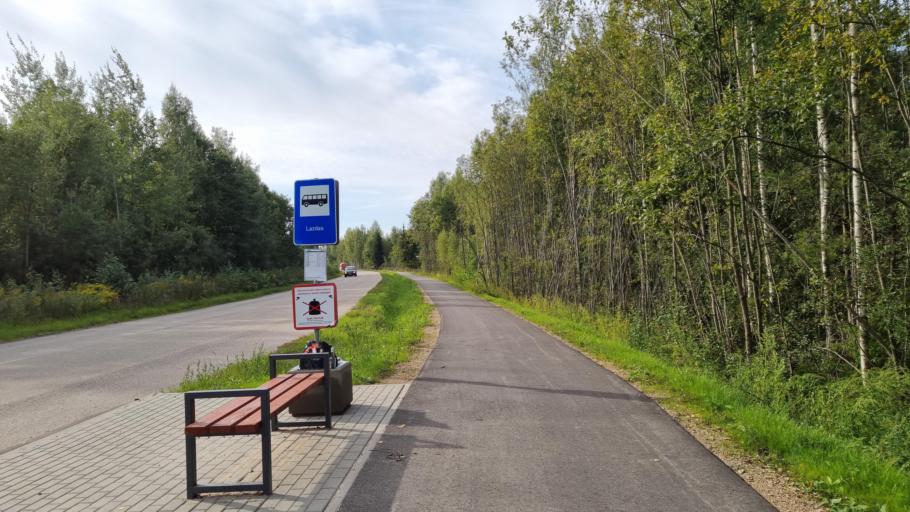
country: LV
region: Lecava
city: Iecava
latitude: 56.6983
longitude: 24.0816
